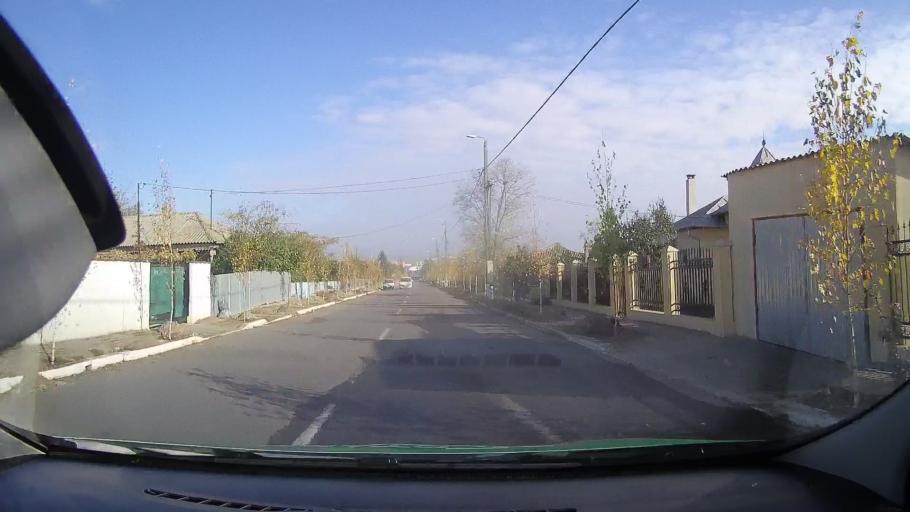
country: RO
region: Tulcea
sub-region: Comuna Mahmudia
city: Mahmudia
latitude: 45.0848
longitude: 29.0842
